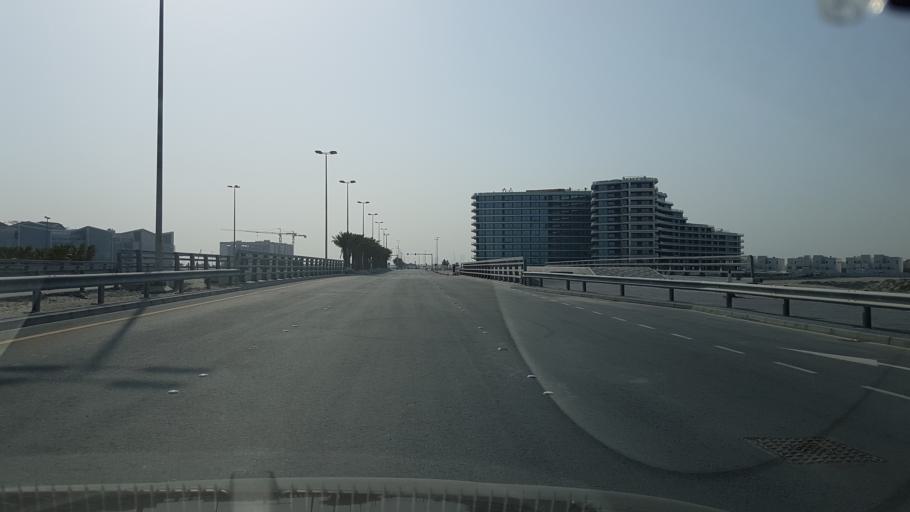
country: BH
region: Muharraq
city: Al Hadd
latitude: 26.2750
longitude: 50.6761
